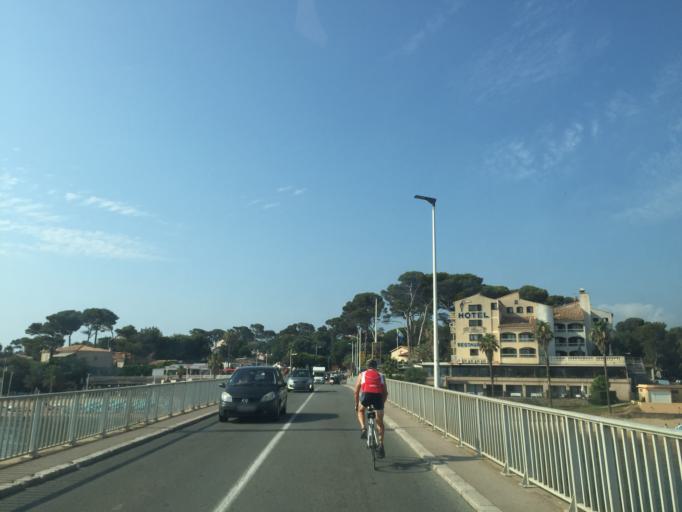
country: FR
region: Provence-Alpes-Cote d'Azur
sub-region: Departement du Var
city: Frejus
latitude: 43.3935
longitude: 6.7283
